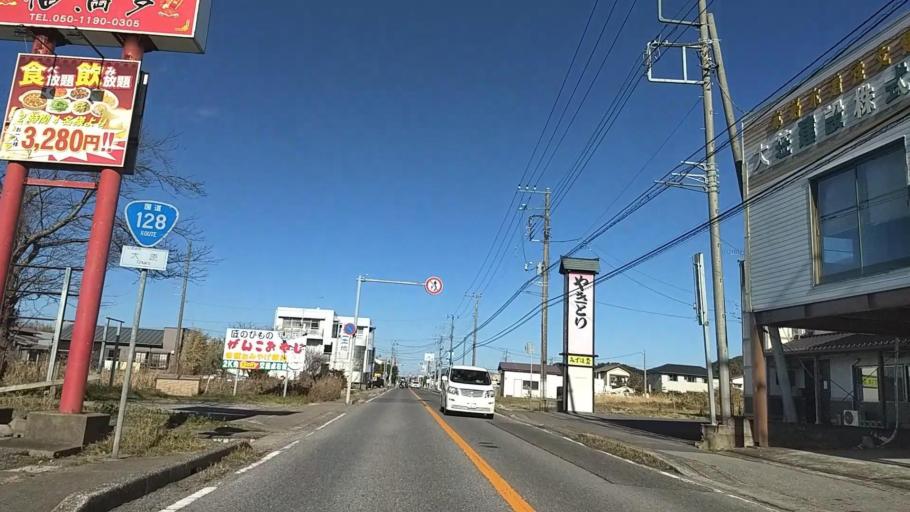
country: JP
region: Chiba
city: Ohara
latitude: 35.2387
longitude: 140.3910
